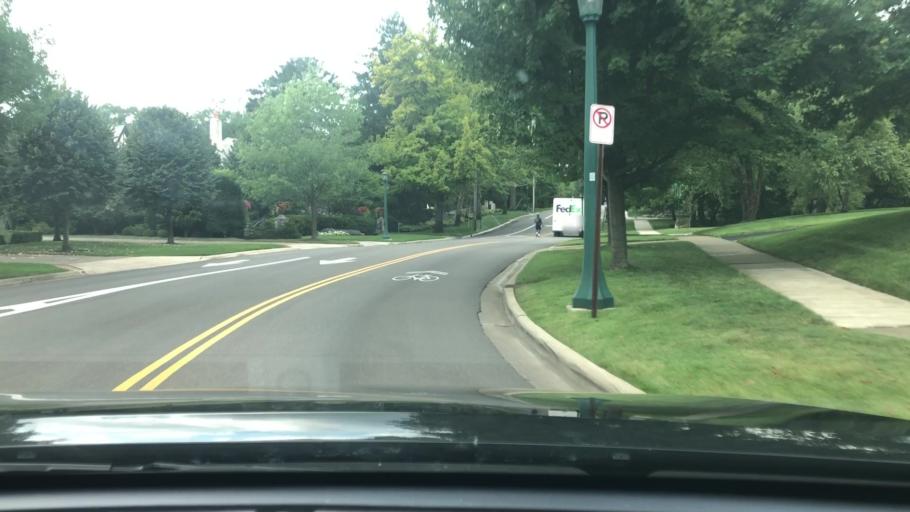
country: US
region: Ohio
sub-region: Franklin County
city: Upper Arlington
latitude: 40.0054
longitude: -83.0694
